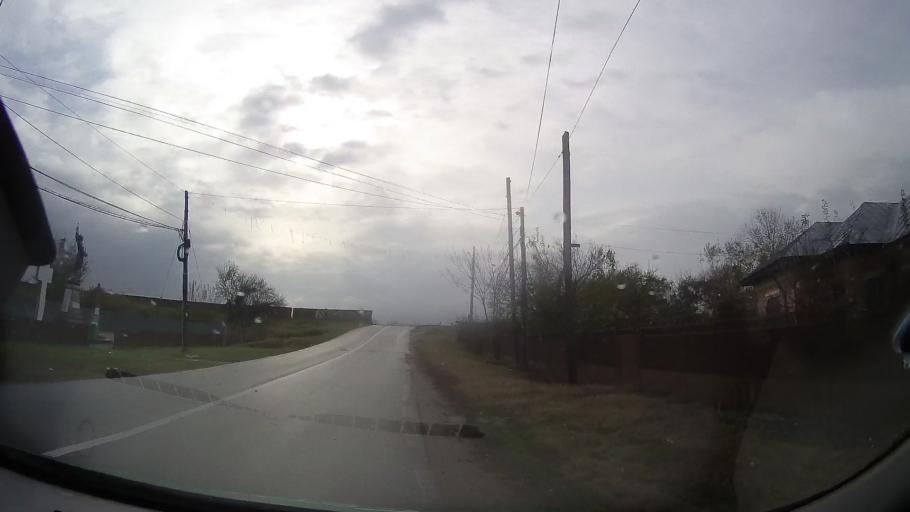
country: RO
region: Ialomita
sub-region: Comuna Fierbinti-Targ
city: Fierbintii de Jos
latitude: 44.6903
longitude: 26.3945
